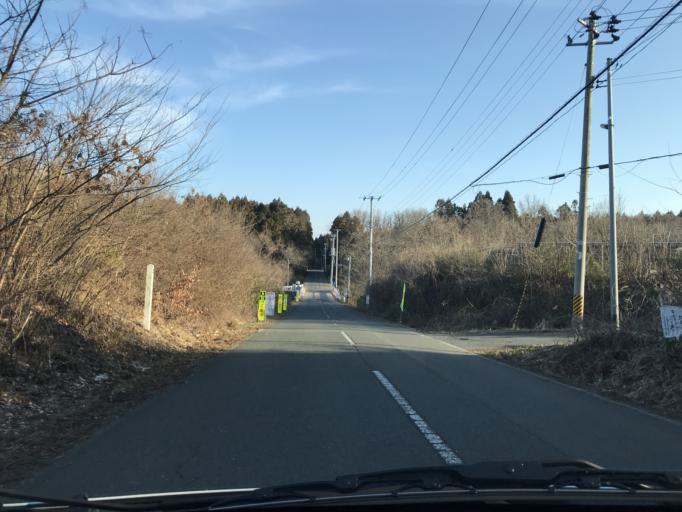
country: JP
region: Iwate
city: Kitakami
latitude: 39.2234
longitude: 141.1036
